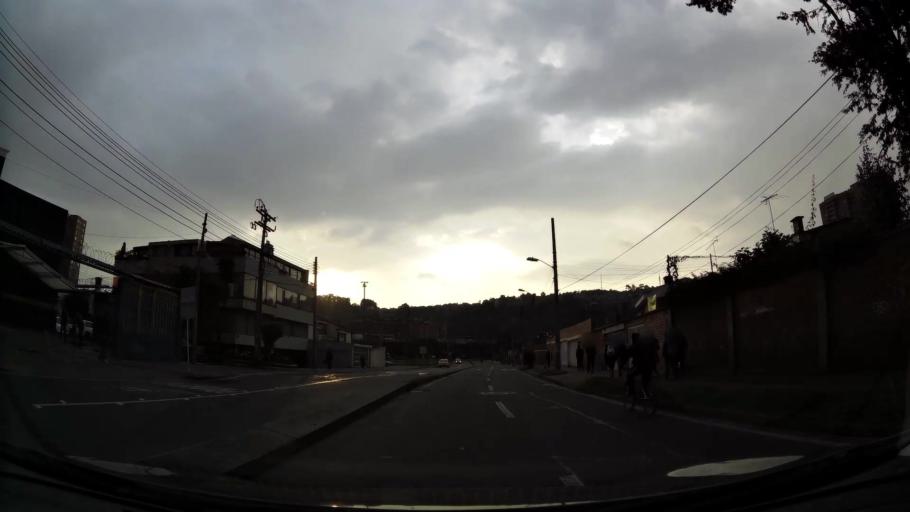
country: CO
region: Bogota D.C.
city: Barrio San Luis
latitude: 4.7196
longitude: -74.0728
